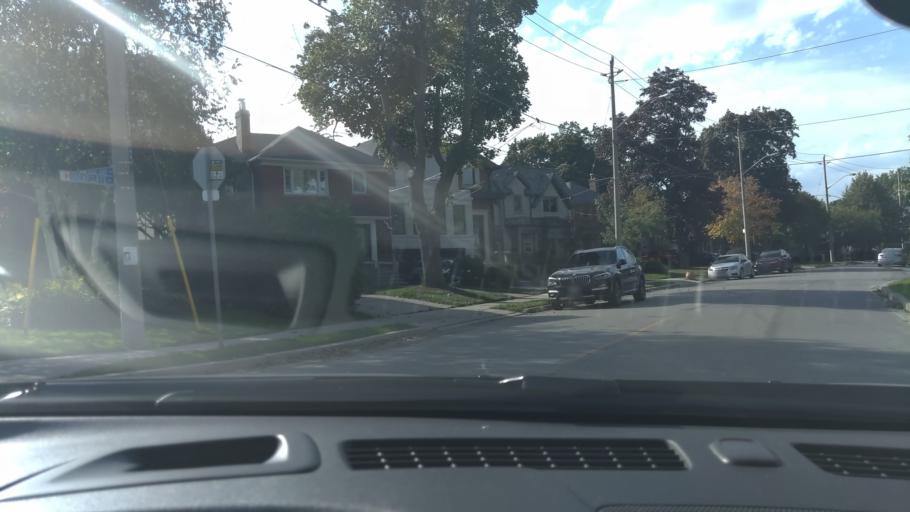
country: CA
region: Ontario
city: Toronto
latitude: 43.7175
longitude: -79.3646
